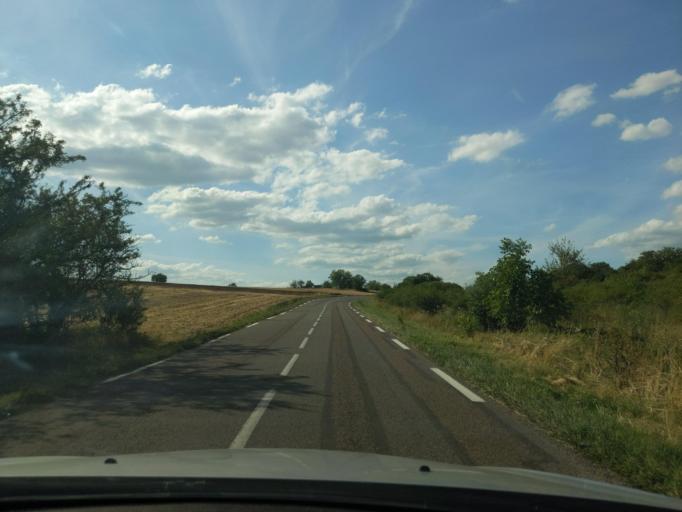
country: FR
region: Bourgogne
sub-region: Departement de la Cote-d'Or
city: Ruffey-les-Echirey
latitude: 47.3714
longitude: 5.0711
